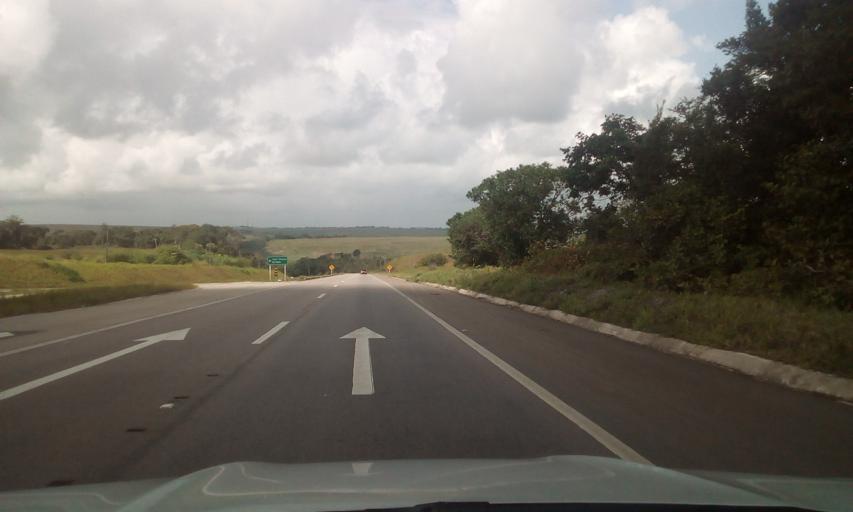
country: BR
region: Paraiba
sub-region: Alhandra
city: Alhandra
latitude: -7.4526
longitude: -34.9809
